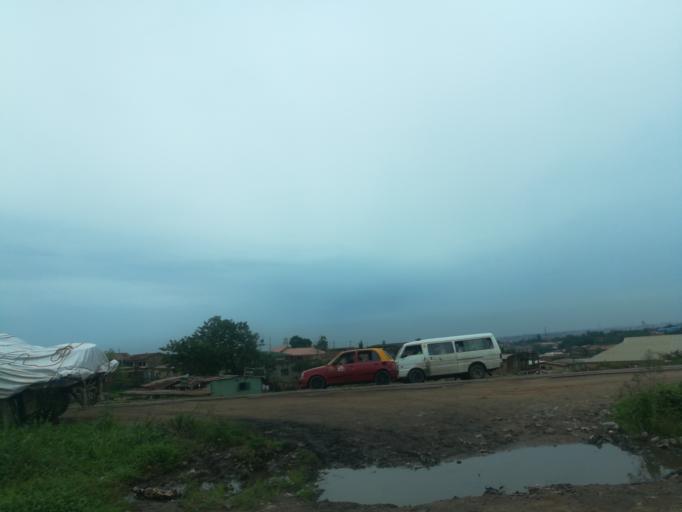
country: NG
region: Oyo
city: Ibadan
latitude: 7.3467
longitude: 3.9193
